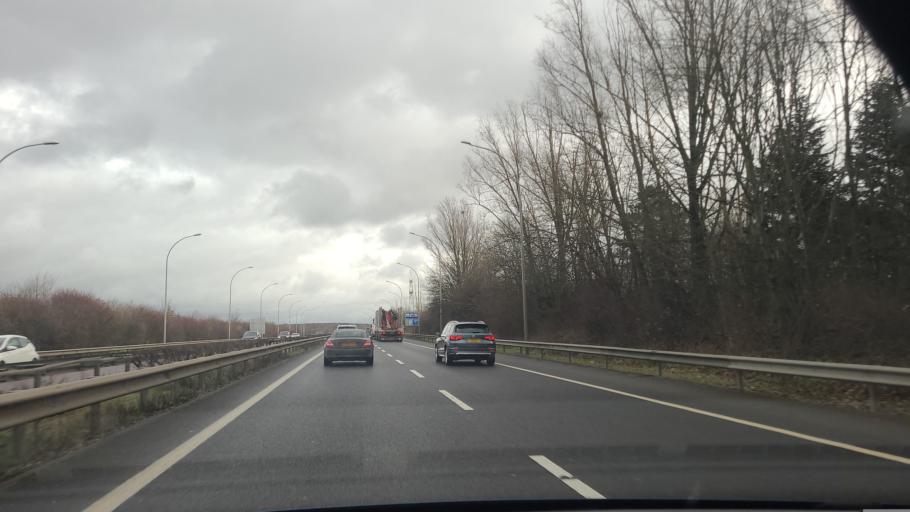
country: LU
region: Luxembourg
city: Pontpierre
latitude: 49.5424
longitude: 6.0347
